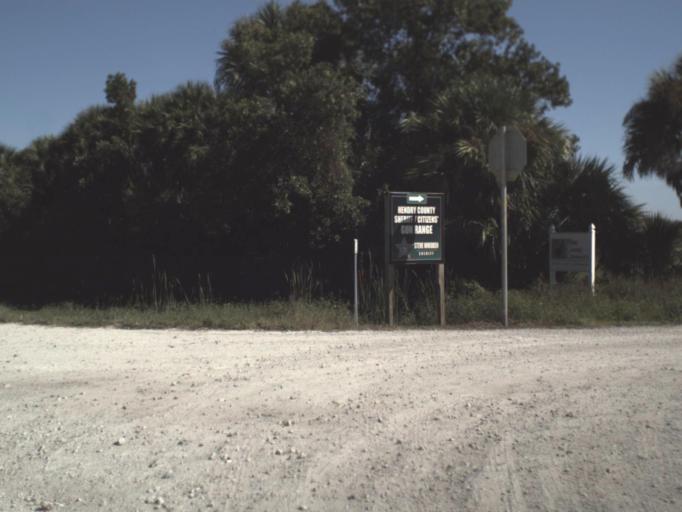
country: US
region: Florida
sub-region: Glades County
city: Moore Haven
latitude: 26.7683
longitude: -81.2045
